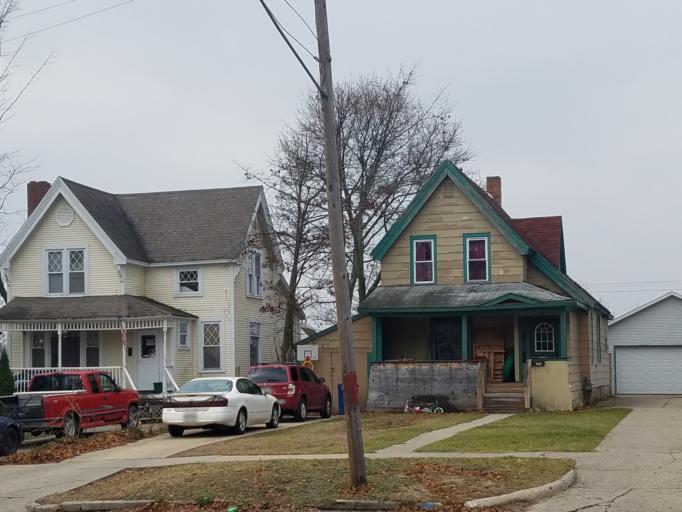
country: US
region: Michigan
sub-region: Wexford County
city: Cadillac
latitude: 44.2533
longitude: -85.3932
